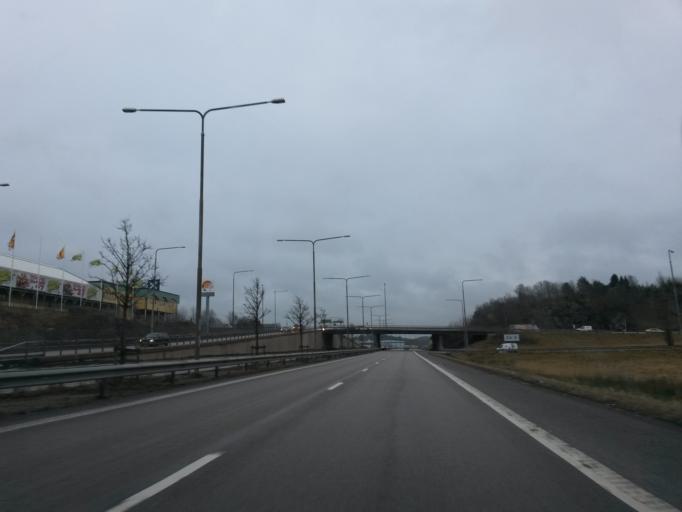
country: SE
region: Vaestra Goetaland
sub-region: Uddevalla Kommun
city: Uddevalla
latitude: 58.3551
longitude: 11.9604
